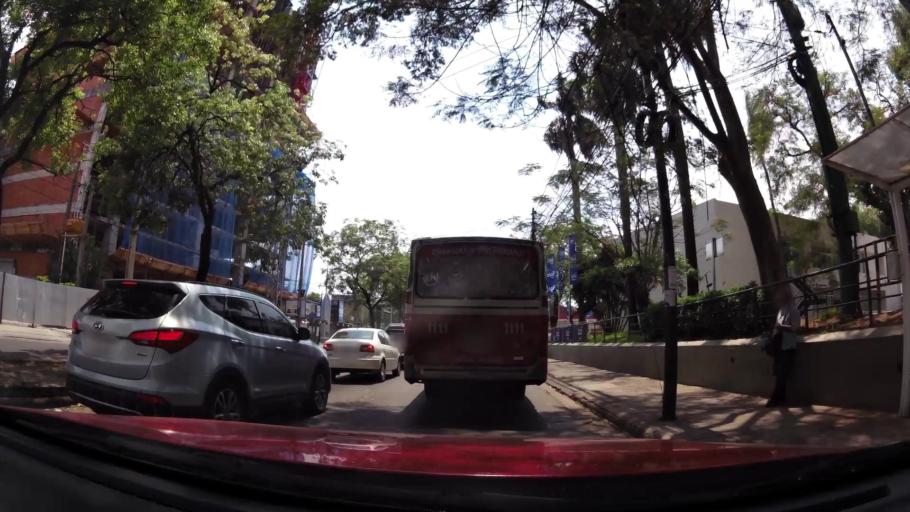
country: PY
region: Central
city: Lambare
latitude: -25.2959
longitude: -57.5775
